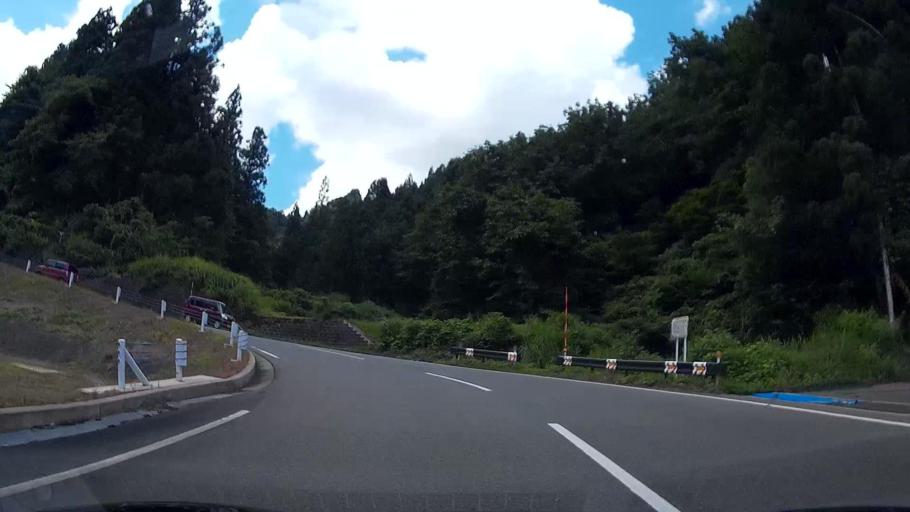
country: JP
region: Niigata
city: Shiozawa
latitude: 37.0219
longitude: 138.8118
